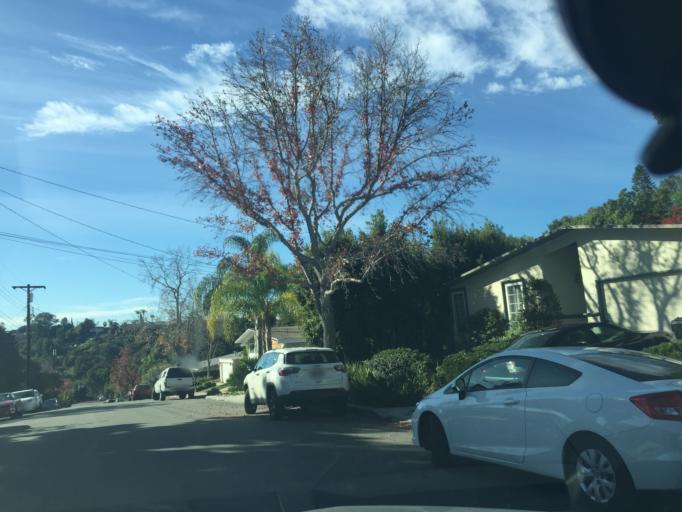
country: US
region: California
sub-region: San Diego County
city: Lemon Grove
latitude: 32.7697
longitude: -117.0790
